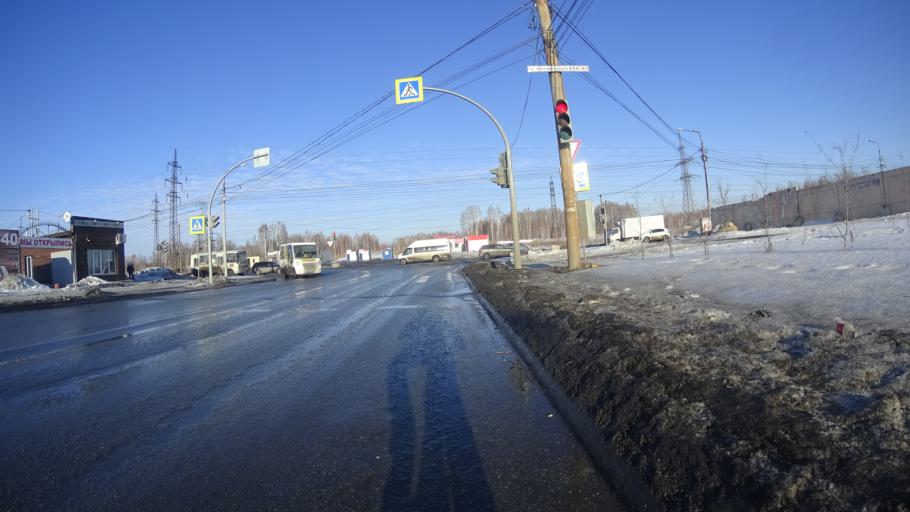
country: RU
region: Chelyabinsk
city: Roshchino
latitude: 55.2204
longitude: 61.2961
